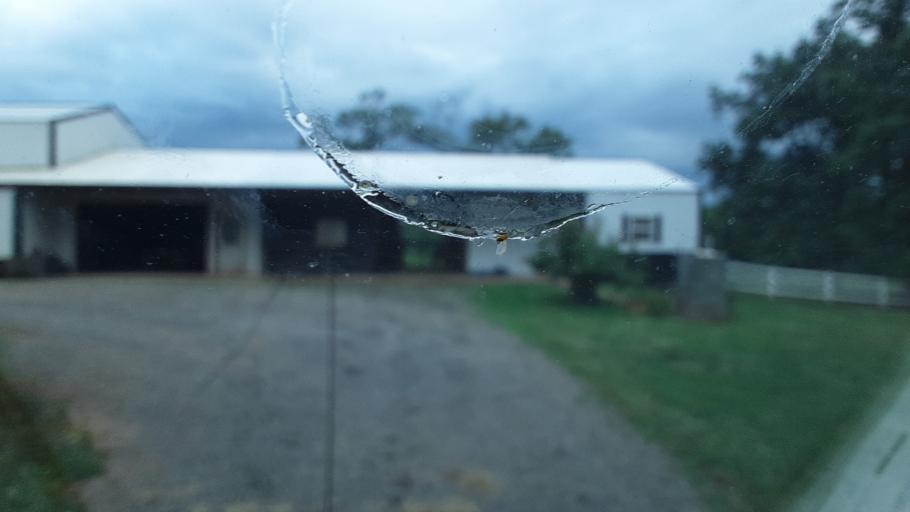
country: US
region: North Carolina
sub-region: Yadkin County
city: Yadkinville
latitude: 36.0509
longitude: -80.8257
